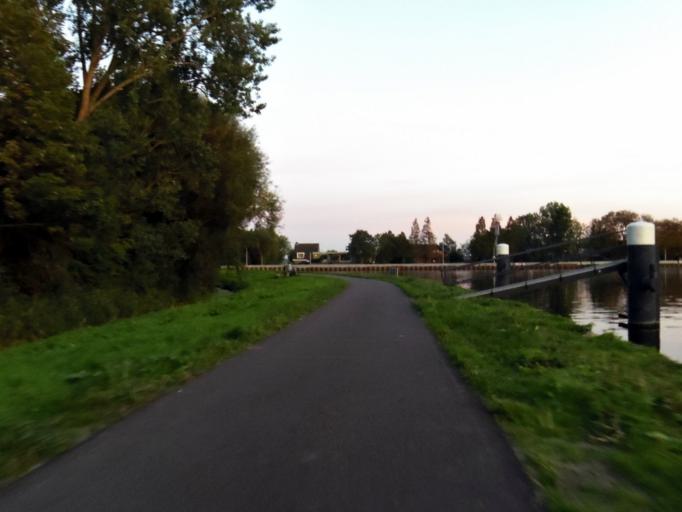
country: NL
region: South Holland
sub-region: Gemeente Voorschoten
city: Voorschoten
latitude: 52.1347
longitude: 4.4693
